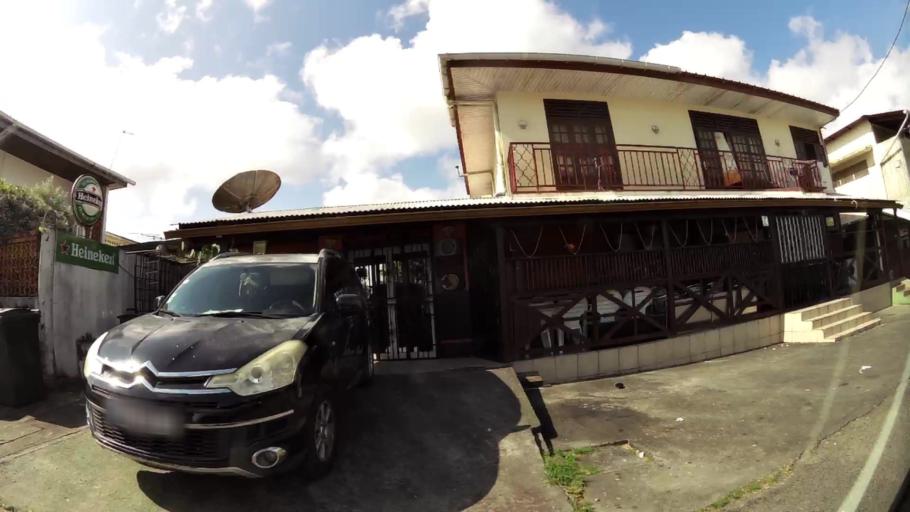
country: GF
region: Guyane
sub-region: Guyane
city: Cayenne
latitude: 4.9374
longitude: -52.3184
